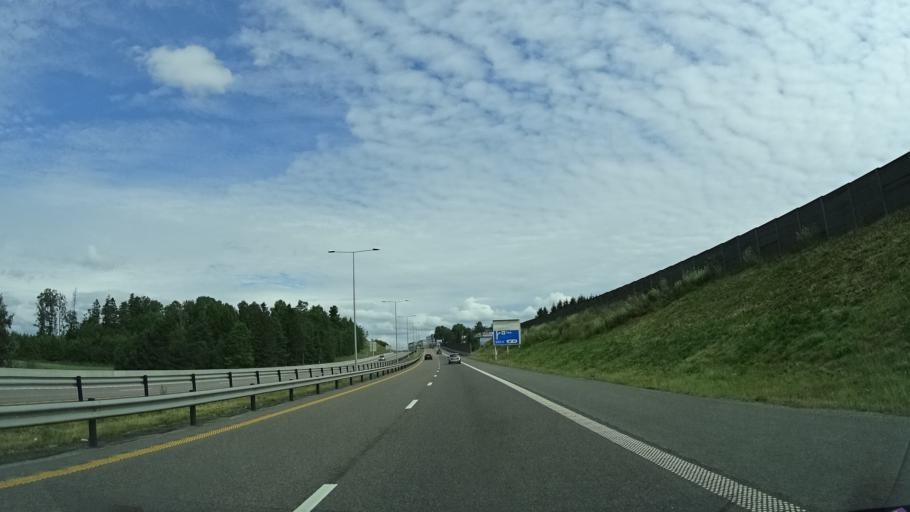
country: NO
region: Vestfold
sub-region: Sandefjord
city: Sandefjord
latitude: 59.1688
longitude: 10.2045
